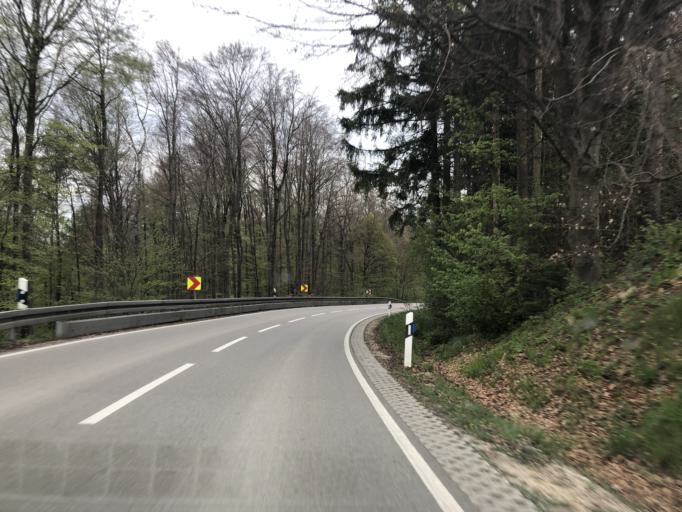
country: DE
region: Bavaria
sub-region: Upper Bavaria
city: Kirchdorf
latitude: 48.4404
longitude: 11.6777
